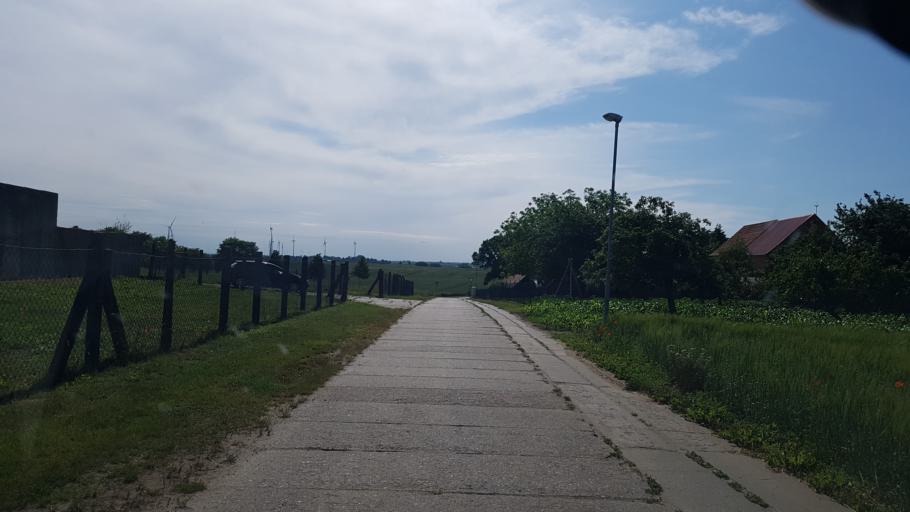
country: DE
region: Brandenburg
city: Gramzow
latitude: 53.2611
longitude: 13.9758
